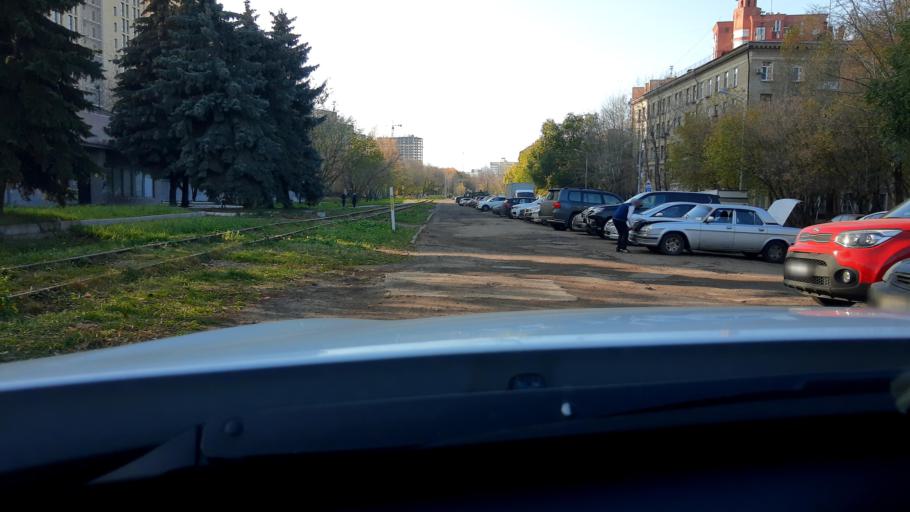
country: RU
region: Moskovskaya
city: Khoroshevo-Mnevniki
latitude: 55.7882
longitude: 37.4950
